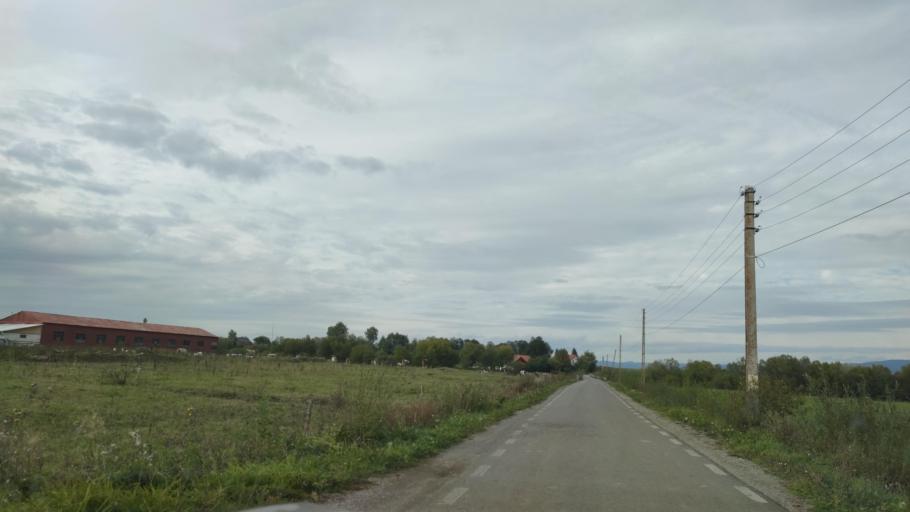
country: RO
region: Harghita
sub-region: Comuna Remetea
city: Remetea
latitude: 46.8106
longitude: 25.4228
